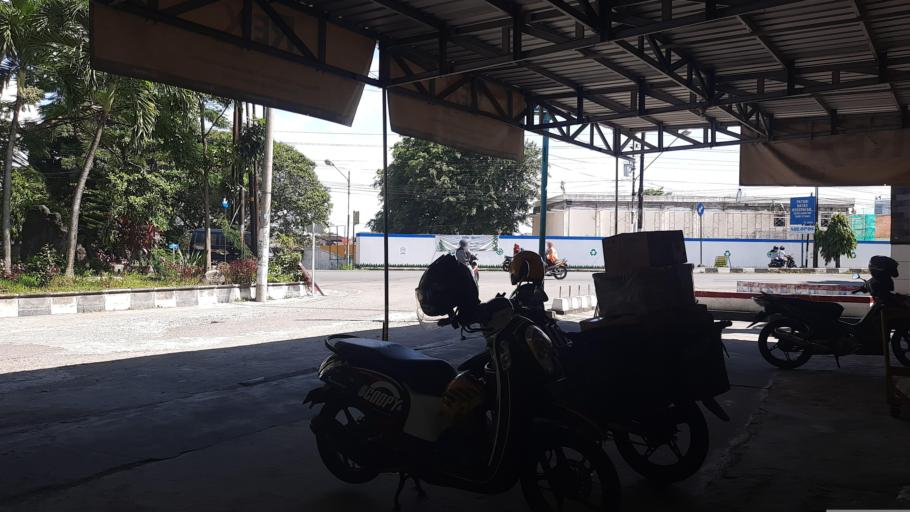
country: ID
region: Central Java
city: Surakarta
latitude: -7.5567
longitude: 110.7959
